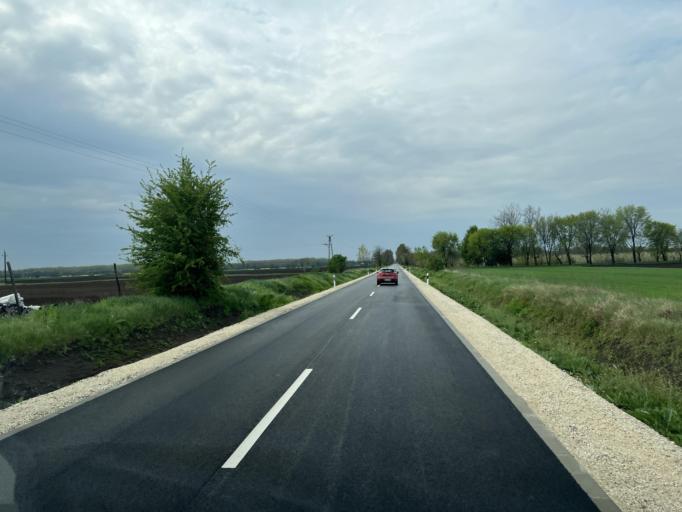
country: HU
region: Pest
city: Nyaregyhaza
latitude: 47.2414
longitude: 19.5203
